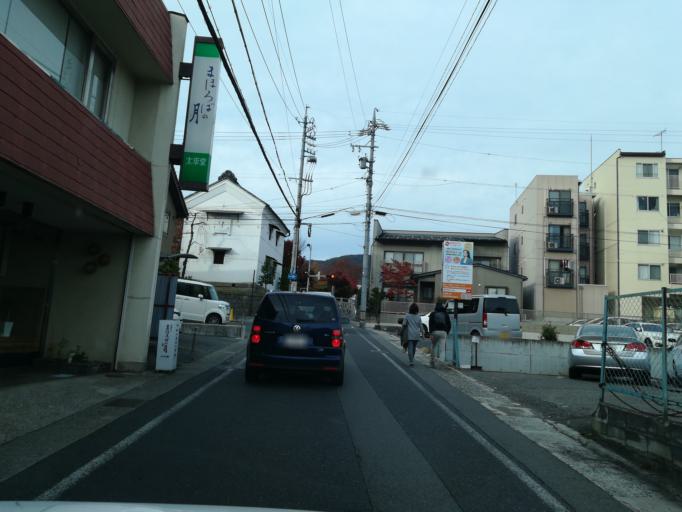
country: JP
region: Nagano
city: Nagano-shi
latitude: 36.6556
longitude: 138.1840
